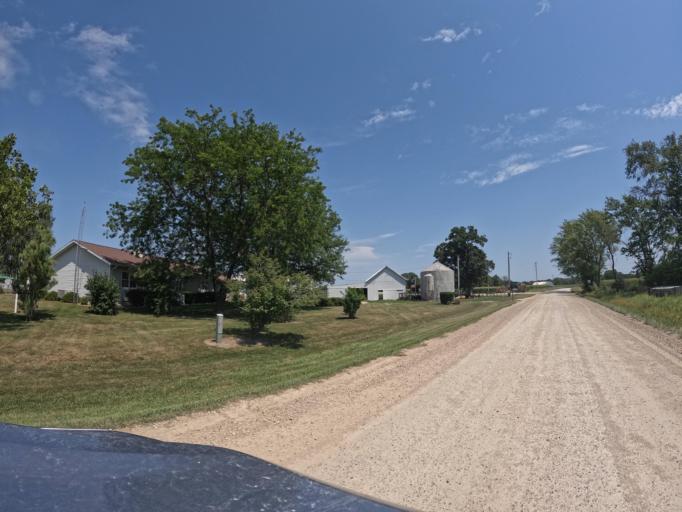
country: US
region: Iowa
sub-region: Henry County
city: Mount Pleasant
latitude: 40.8938
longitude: -91.6973
